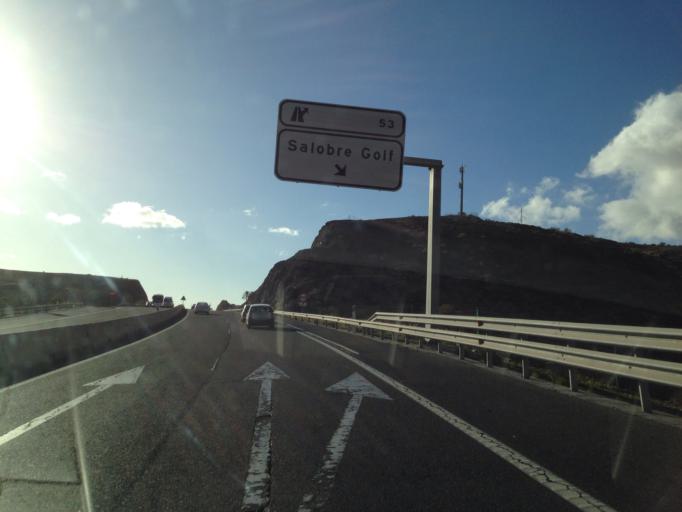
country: ES
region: Canary Islands
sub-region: Provincia de Las Palmas
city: Maspalomas
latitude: 27.7713
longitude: -15.6381
